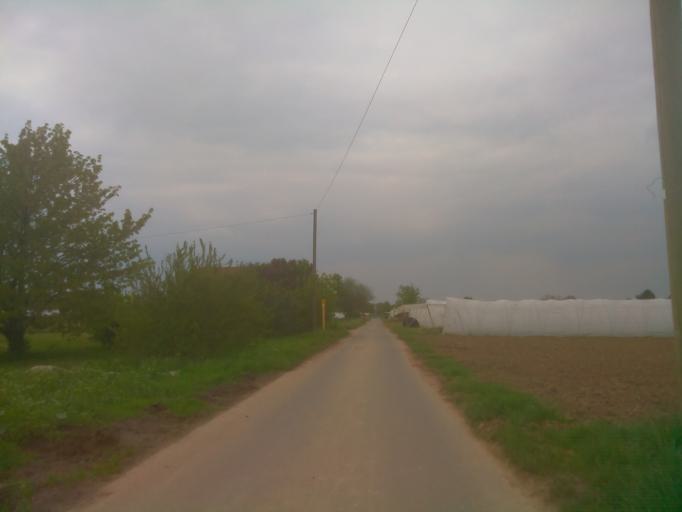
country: DE
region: Baden-Wuerttemberg
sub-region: Karlsruhe Region
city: Dossenheim
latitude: 49.4347
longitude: 8.6707
